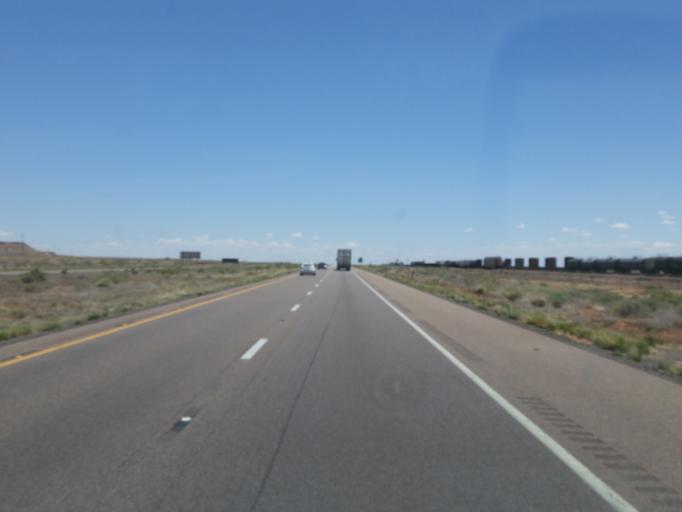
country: US
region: Arizona
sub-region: Coconino County
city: LeChee
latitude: 35.0748
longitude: -110.8611
